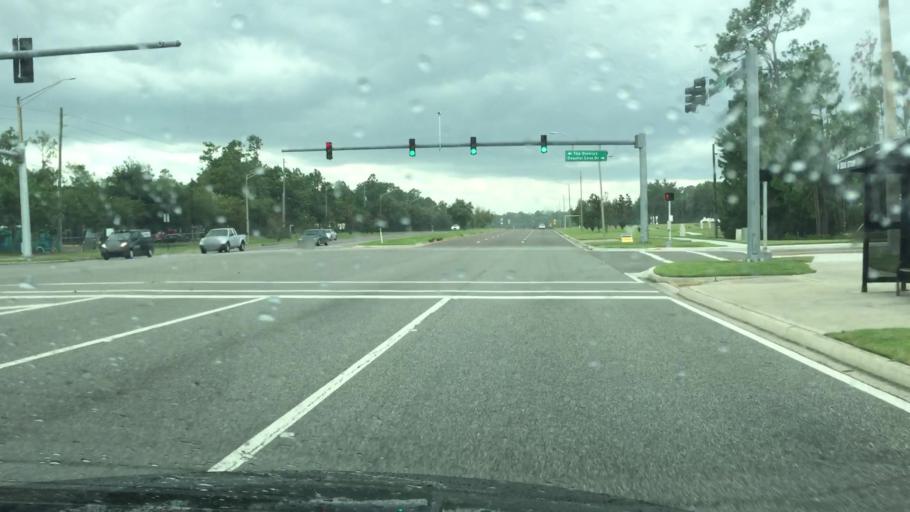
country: US
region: Florida
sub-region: Duval County
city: Jacksonville Beach
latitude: 30.2811
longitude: -81.4921
